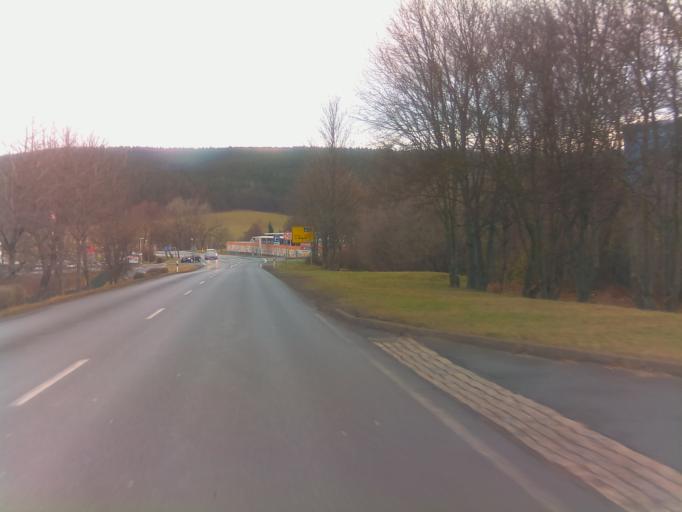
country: DE
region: Thuringia
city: Unterwellenborn
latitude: 50.6570
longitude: 11.4495
